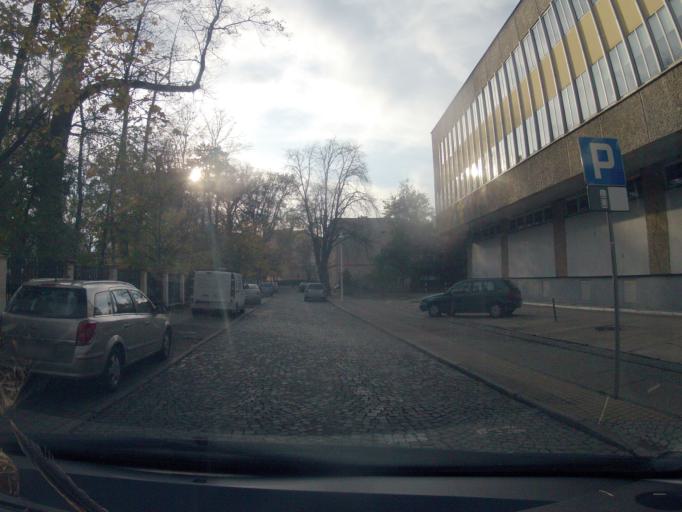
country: PL
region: Opole Voivodeship
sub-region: Powiat opolski
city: Opole
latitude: 50.6657
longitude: 17.9214
